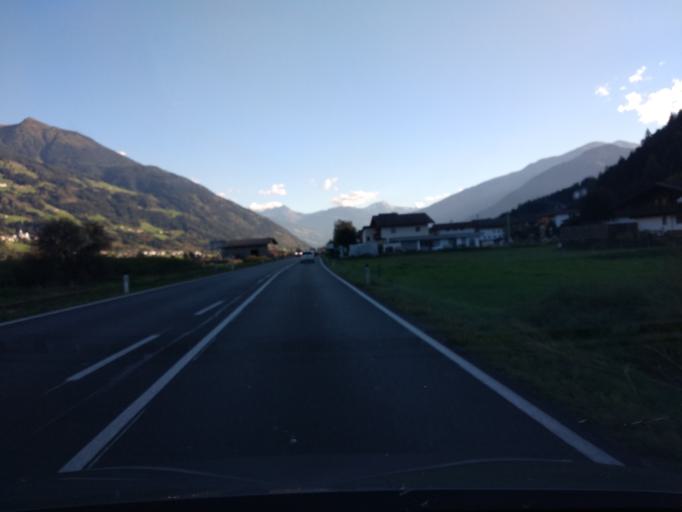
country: AT
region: Tyrol
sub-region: Politischer Bezirk Schwaz
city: Fugenberg
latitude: 47.3653
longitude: 11.8506
